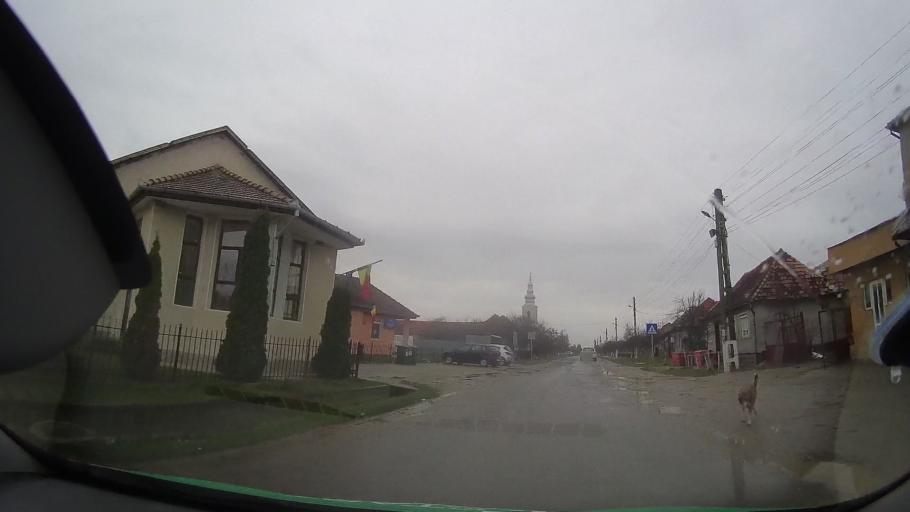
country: RO
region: Bihor
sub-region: Comuna Olcea
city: Olcea
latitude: 46.6827
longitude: 21.9811
